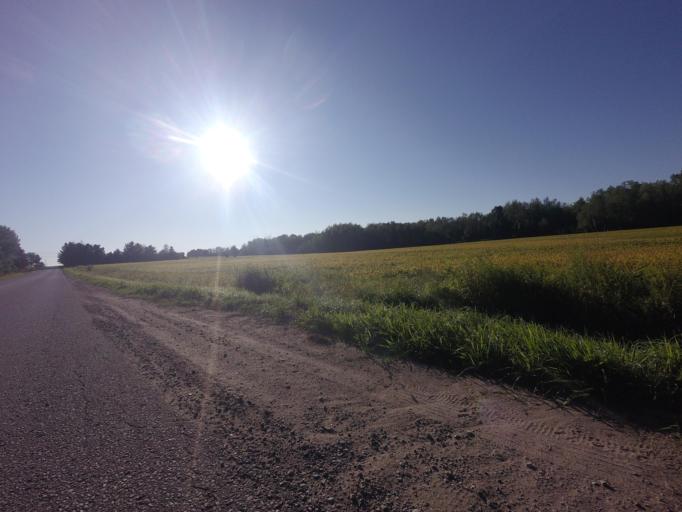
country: CA
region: Ontario
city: Bradford West Gwillimbury
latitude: 44.0511
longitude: -79.7329
